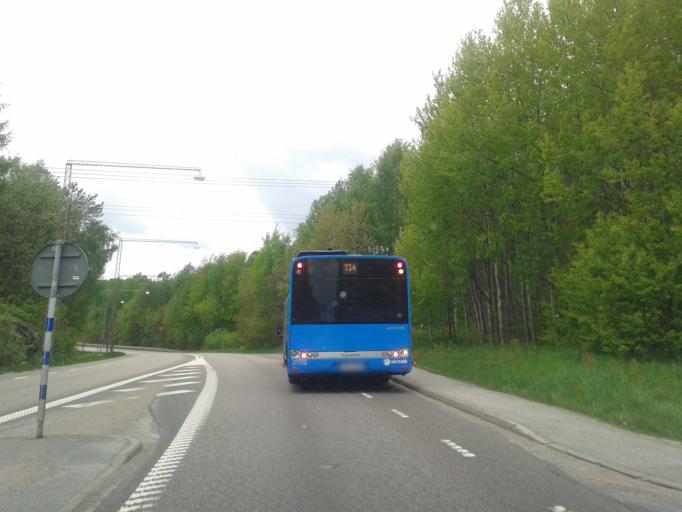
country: SE
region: Vaestra Goetaland
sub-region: Goteborg
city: Gardsten
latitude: 57.7975
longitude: 12.0373
